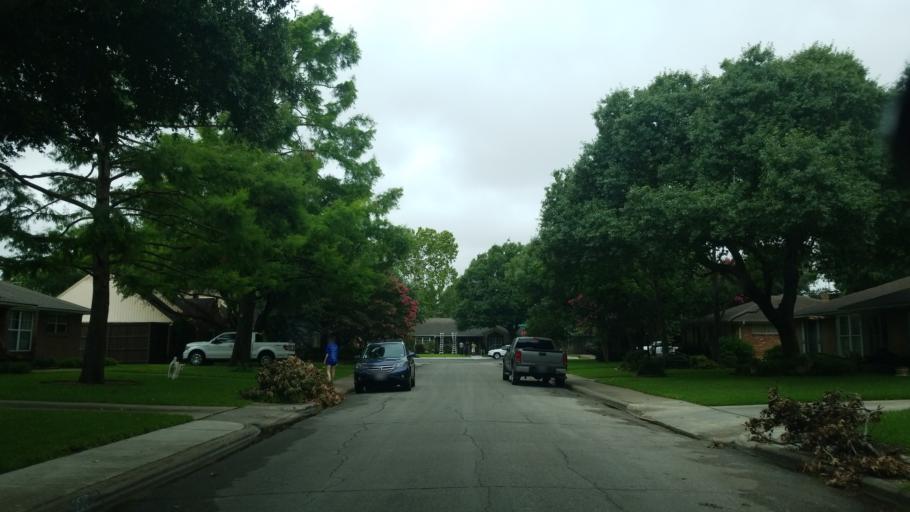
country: US
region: Texas
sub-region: Dallas County
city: Farmers Branch
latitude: 32.8933
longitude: -96.8615
